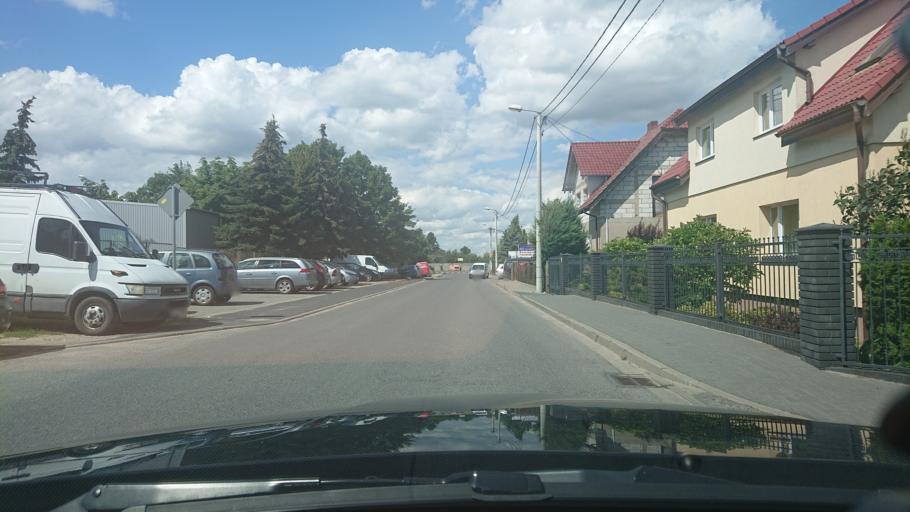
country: PL
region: Greater Poland Voivodeship
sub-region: Powiat gnieznienski
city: Gniezno
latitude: 52.5404
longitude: 17.6341
